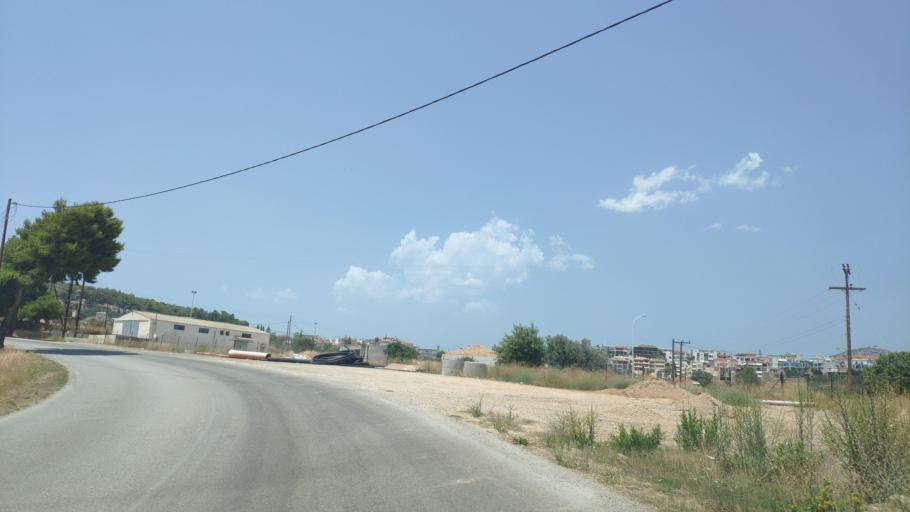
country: GR
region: Peloponnese
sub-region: Nomos Argolidos
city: Kranidi
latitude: 37.3700
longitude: 23.1627
